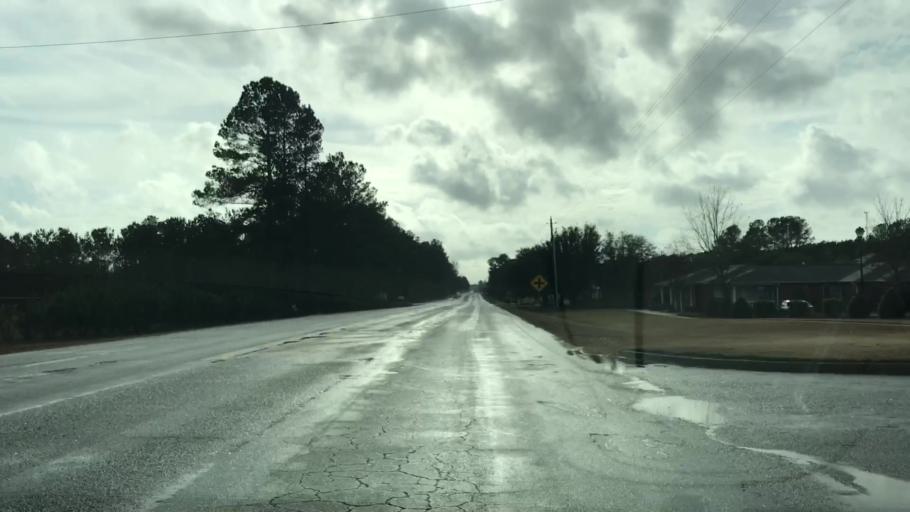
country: US
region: South Carolina
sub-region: Williamsburg County
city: Andrews
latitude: 33.4628
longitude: -79.5706
